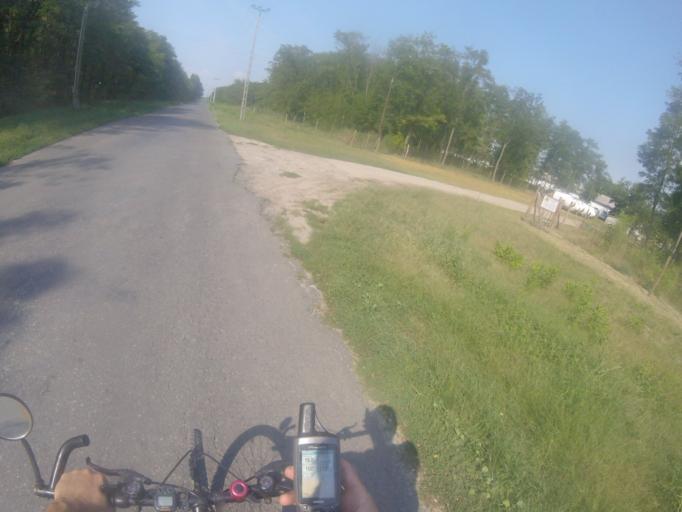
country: HU
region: Bacs-Kiskun
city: Ersekcsanad
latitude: 46.2543
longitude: 18.9622
